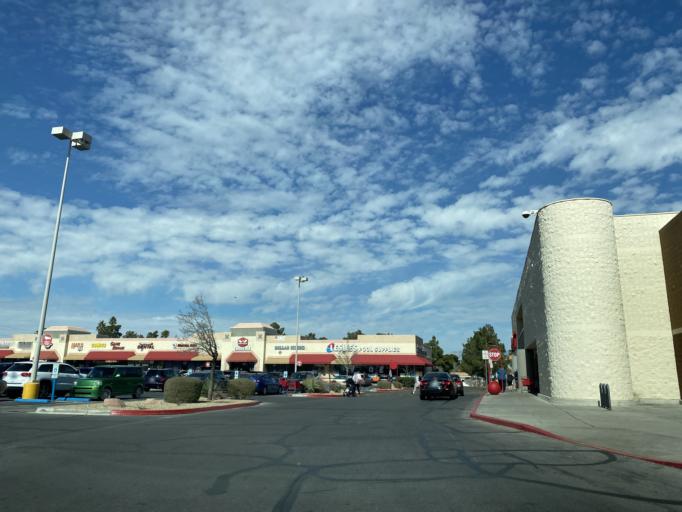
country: US
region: Nevada
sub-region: Clark County
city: Spring Valley
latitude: 36.2191
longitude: -115.2498
